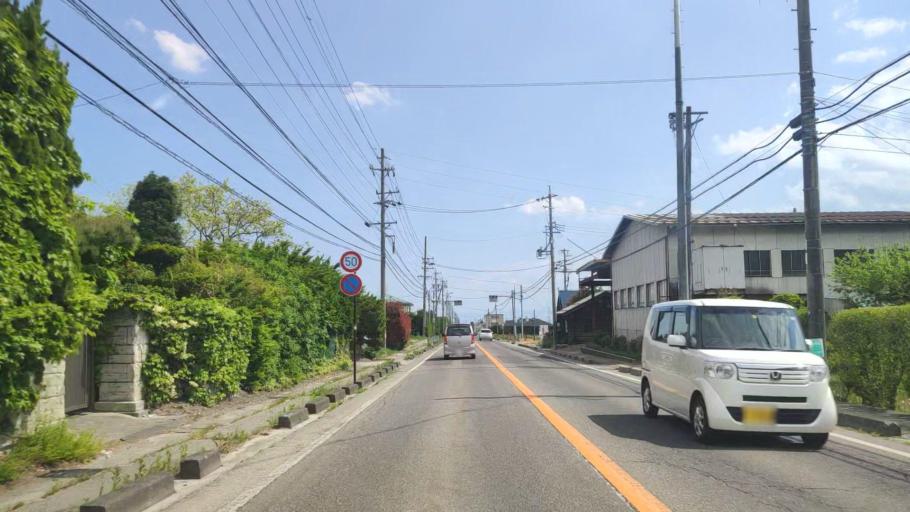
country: JP
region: Nagano
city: Omachi
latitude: 36.4603
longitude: 137.8505
